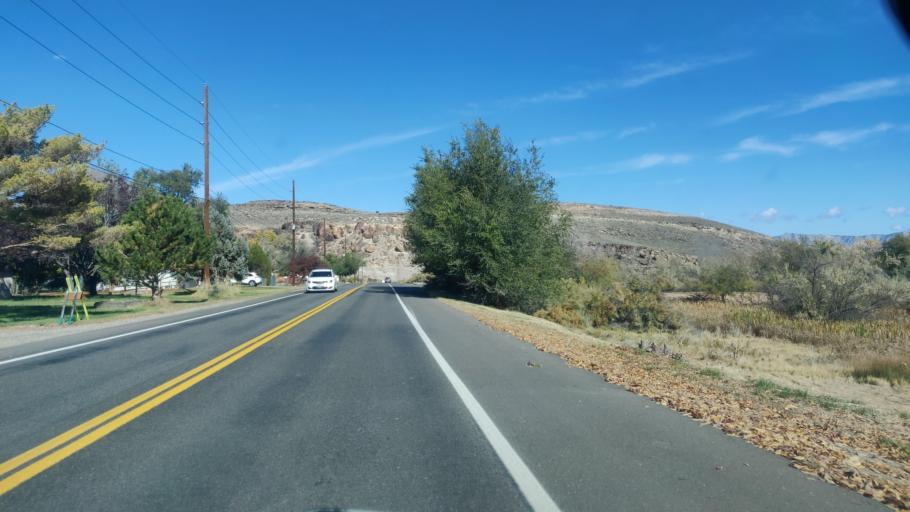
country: US
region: Colorado
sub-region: Mesa County
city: Redlands
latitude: 39.0698
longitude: -108.6449
